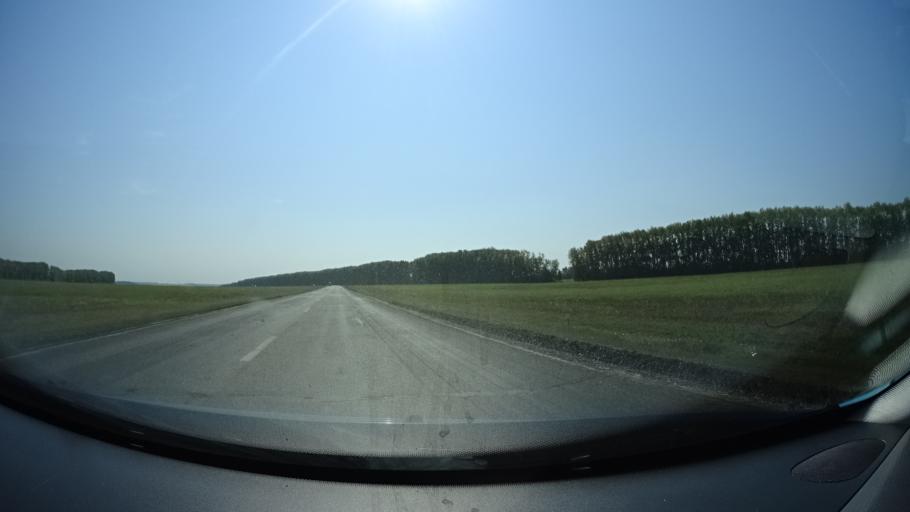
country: RU
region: Bashkortostan
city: Kabakovo
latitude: 54.4546
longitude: 55.9709
